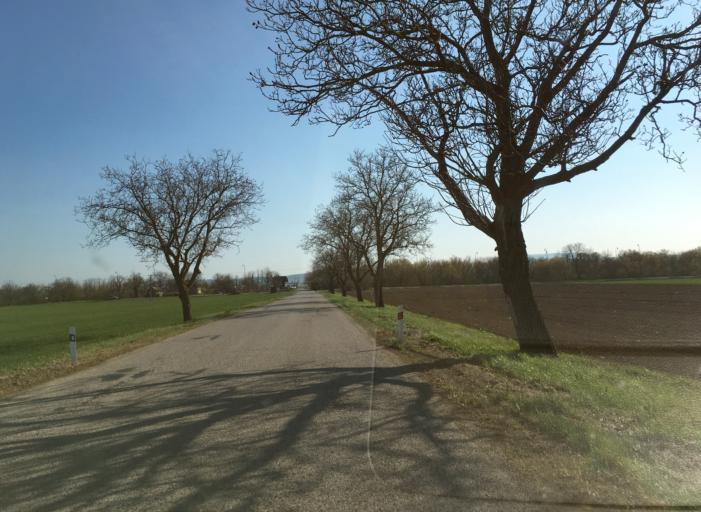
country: HU
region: Komarom-Esztergom
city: Nyergesujfalu
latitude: 47.8147
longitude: 18.6024
